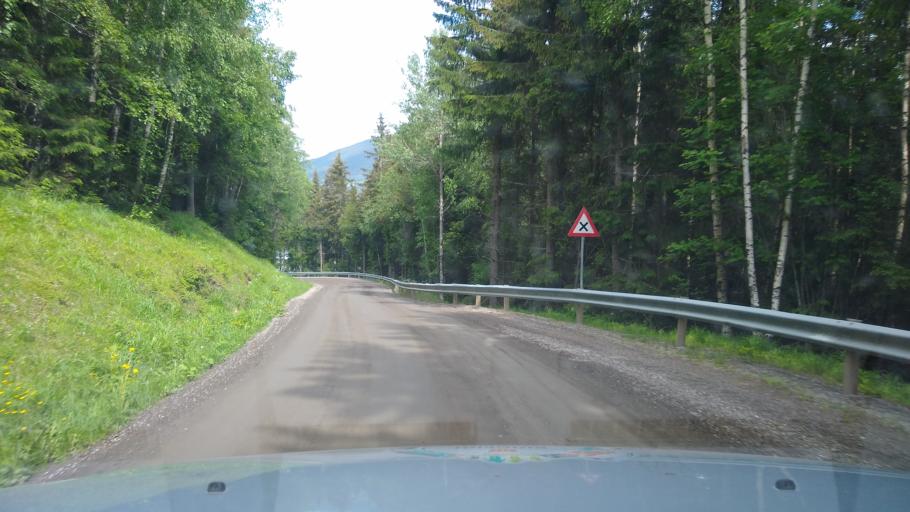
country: NO
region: Oppland
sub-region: Ringebu
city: Ringebu
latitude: 61.5194
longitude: 10.1309
